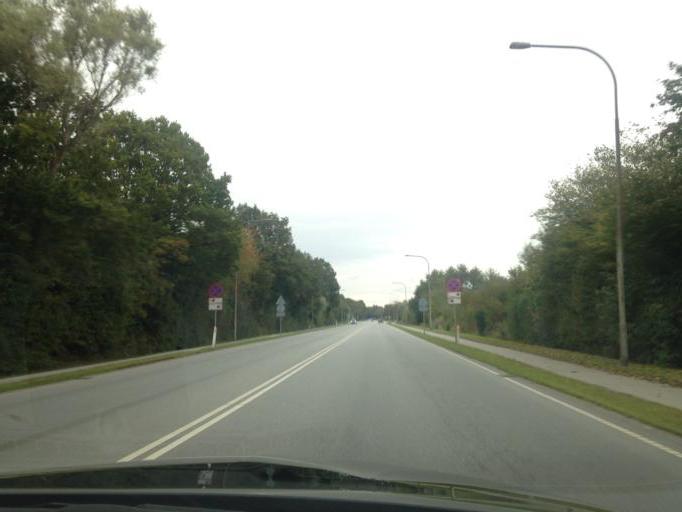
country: DK
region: South Denmark
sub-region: Haderslev Kommune
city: Haderslev
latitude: 55.2608
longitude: 9.4803
